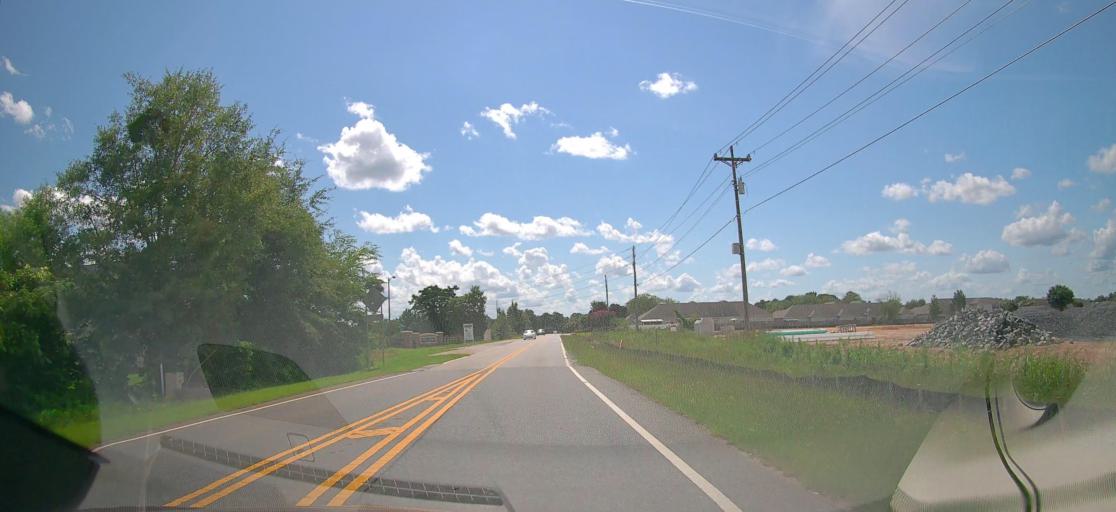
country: US
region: Georgia
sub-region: Houston County
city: Centerville
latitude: 32.6215
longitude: -83.7107
